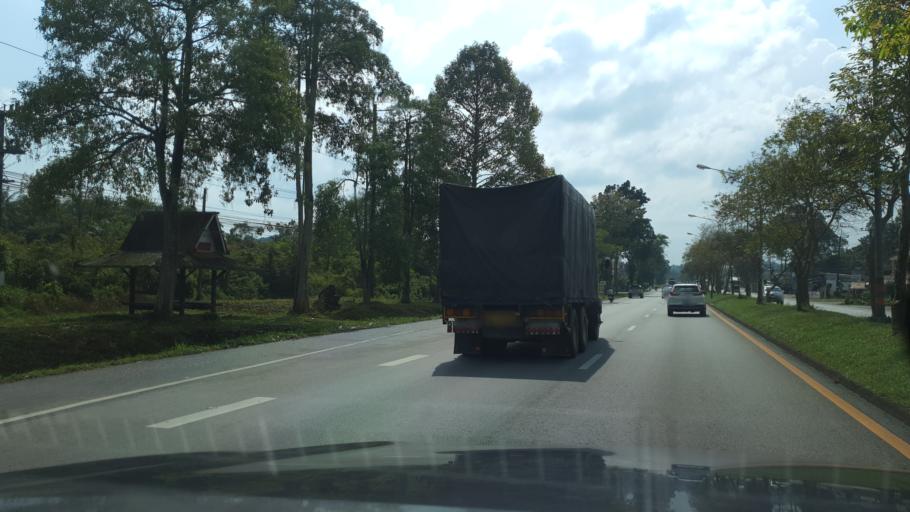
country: TH
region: Chumphon
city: Chumphon
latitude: 10.5679
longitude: 99.1156
